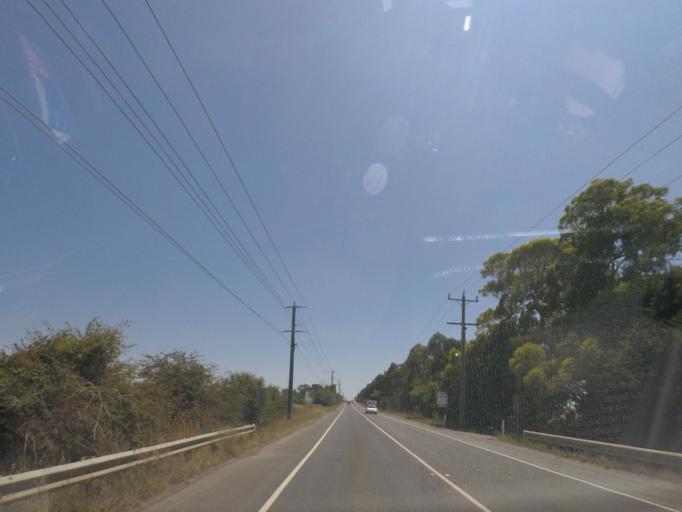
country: AU
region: Victoria
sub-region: Whittlesea
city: Epping
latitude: -37.6065
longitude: 145.0316
